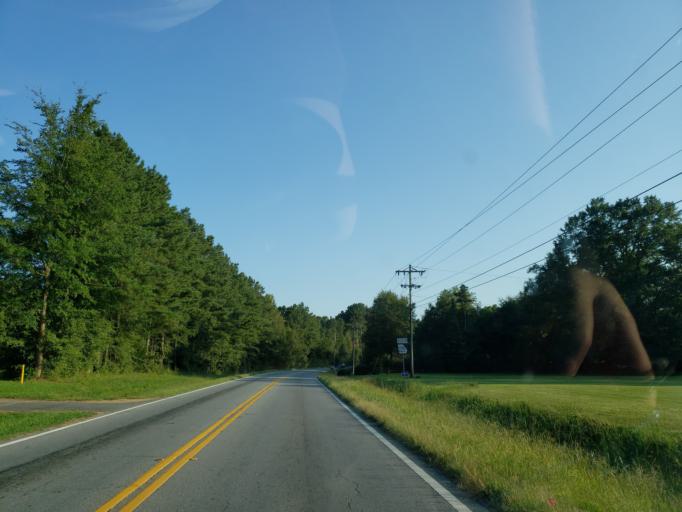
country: US
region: Georgia
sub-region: Murray County
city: Chatsworth
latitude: 34.7029
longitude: -84.8199
